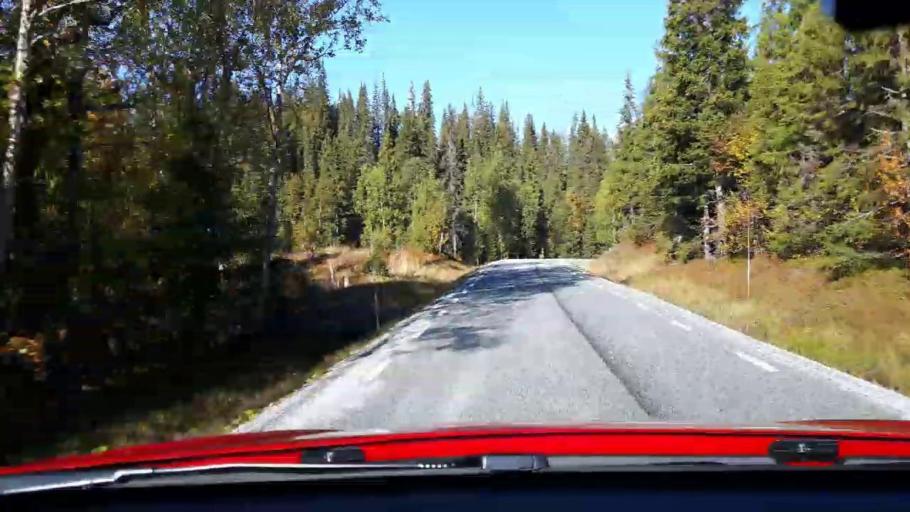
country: NO
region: Nord-Trondelag
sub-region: Lierne
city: Sandvika
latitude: 64.6188
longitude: 13.6988
